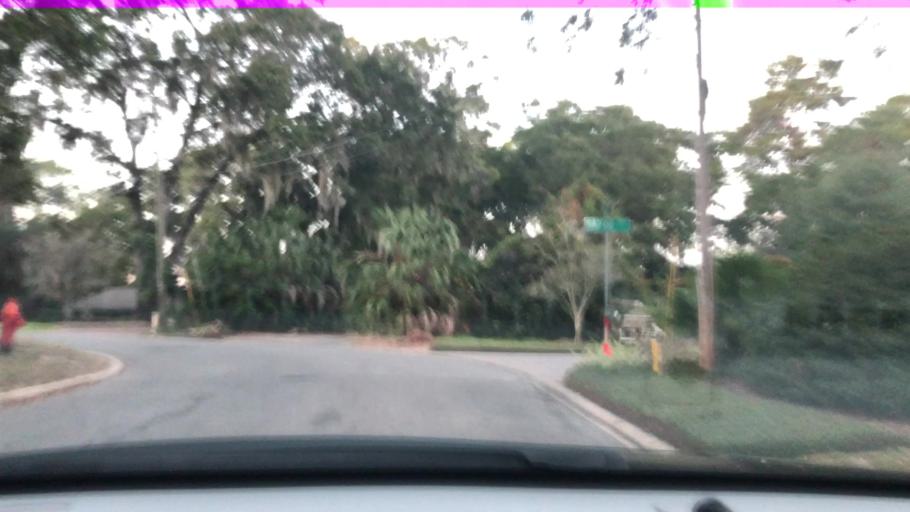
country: US
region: Florida
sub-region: Bay County
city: Panama City
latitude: 30.1399
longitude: -85.6401
